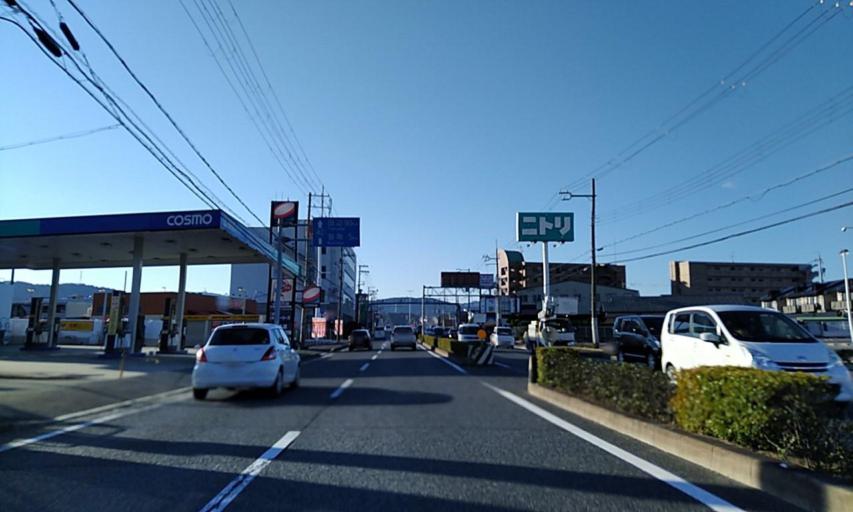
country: JP
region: Wakayama
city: Kainan
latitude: 34.1814
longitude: 135.1861
